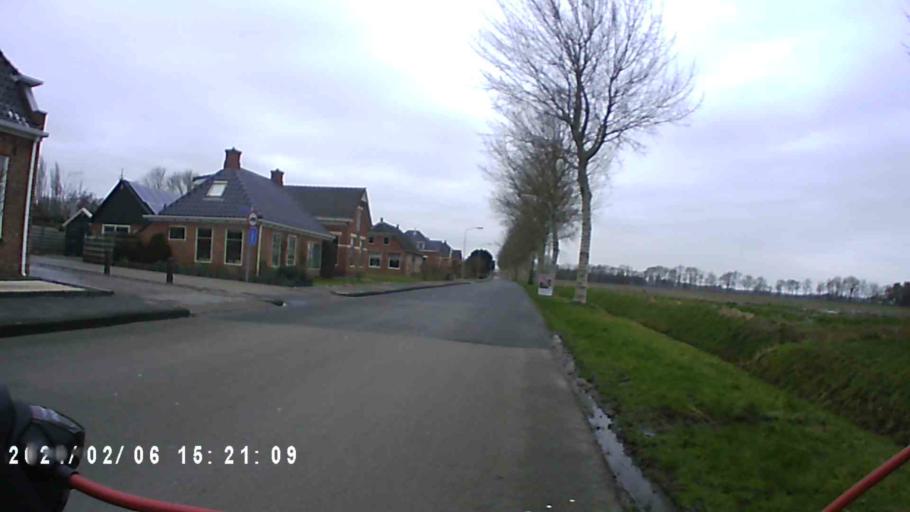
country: NL
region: Groningen
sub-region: Gemeente Bedum
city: Bedum
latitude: 53.4045
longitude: 6.6184
